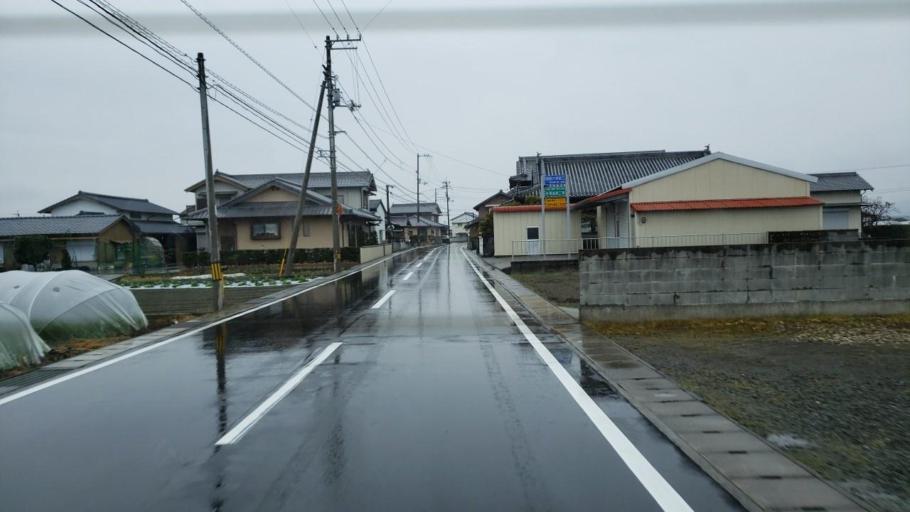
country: JP
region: Tokushima
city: Ishii
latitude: 34.1003
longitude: 134.3977
